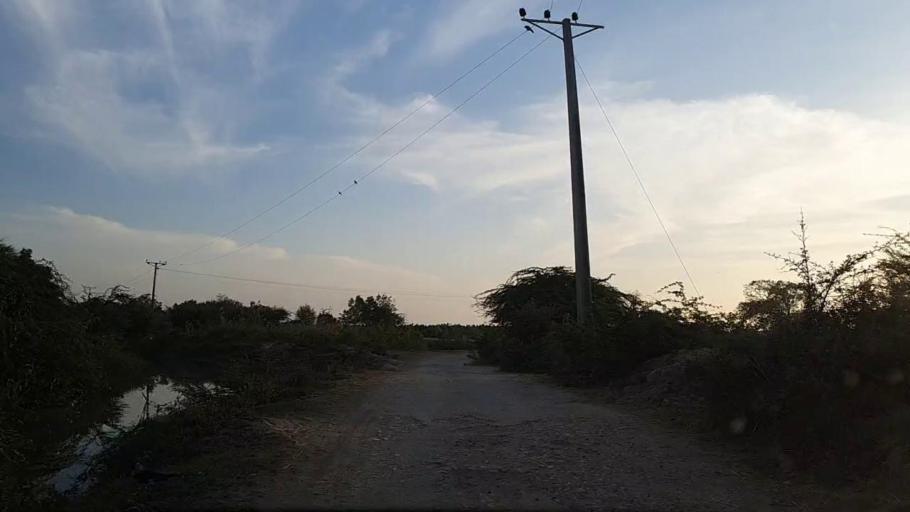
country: PK
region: Sindh
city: Mirpur Batoro
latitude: 24.6347
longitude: 68.1361
